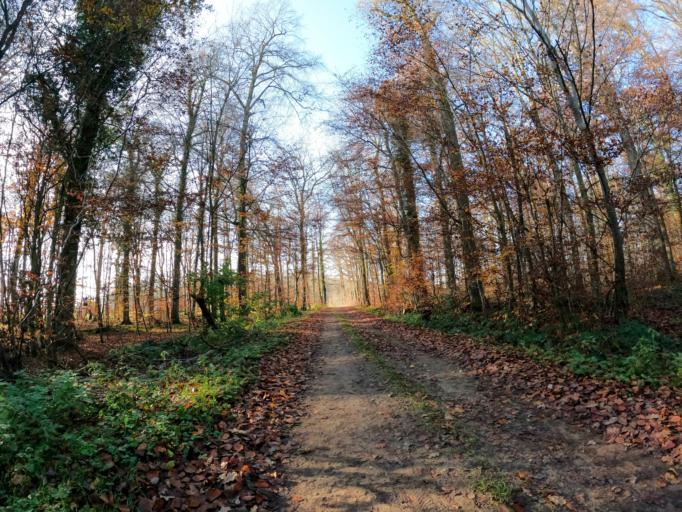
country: LU
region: Luxembourg
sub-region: Canton de Luxembourg
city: Olm
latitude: 49.6799
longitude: 5.9852
